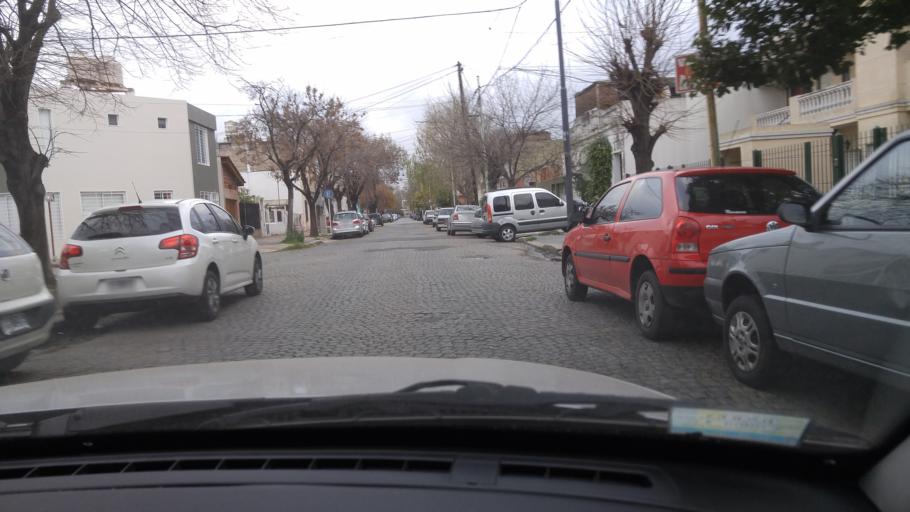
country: AR
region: Buenos Aires
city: Caseros
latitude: -34.6141
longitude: -58.5280
